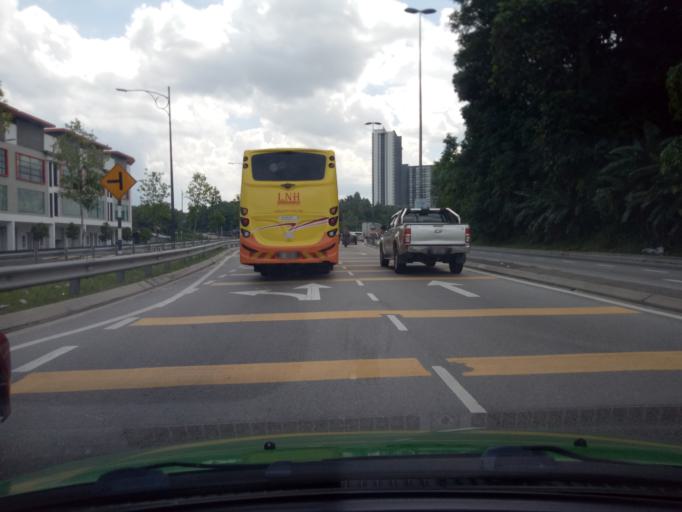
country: MY
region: Selangor
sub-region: Hulu Langat
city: Semenyih
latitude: 2.9583
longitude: 101.8401
